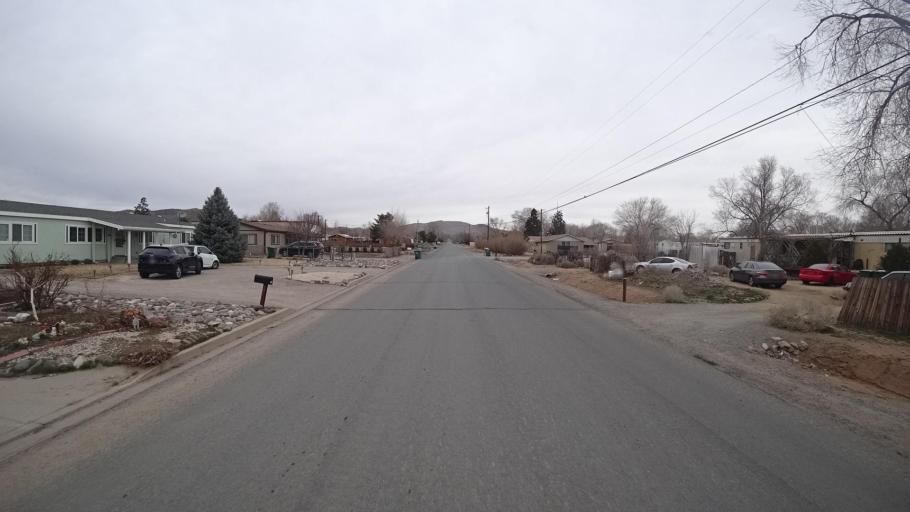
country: US
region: Nevada
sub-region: Washoe County
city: Sun Valley
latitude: 39.5937
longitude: -119.7710
